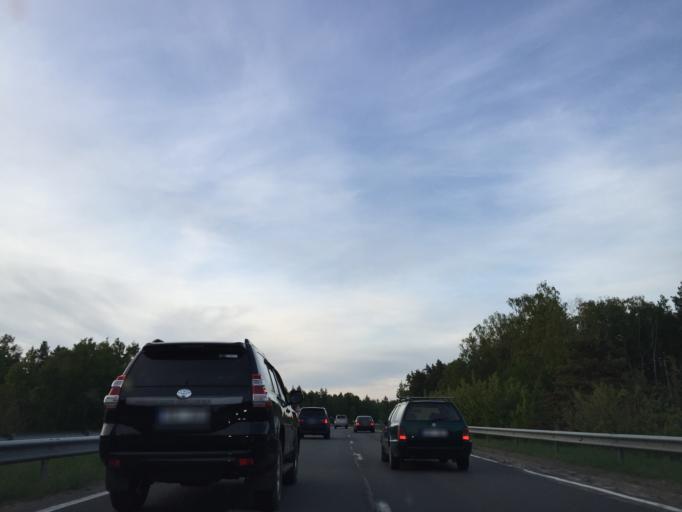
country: LV
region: Babite
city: Pinki
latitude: 56.9601
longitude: 23.9324
